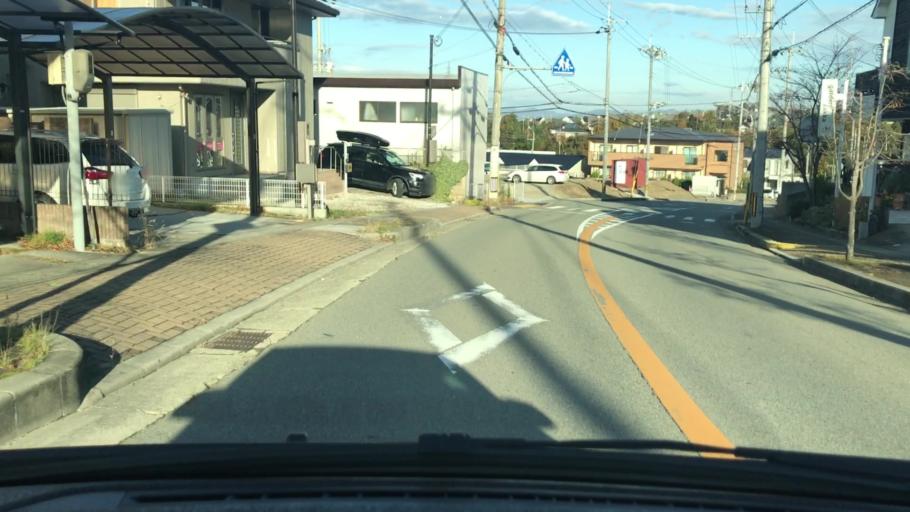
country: JP
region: Hyogo
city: Sandacho
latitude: 34.8265
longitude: 135.2503
